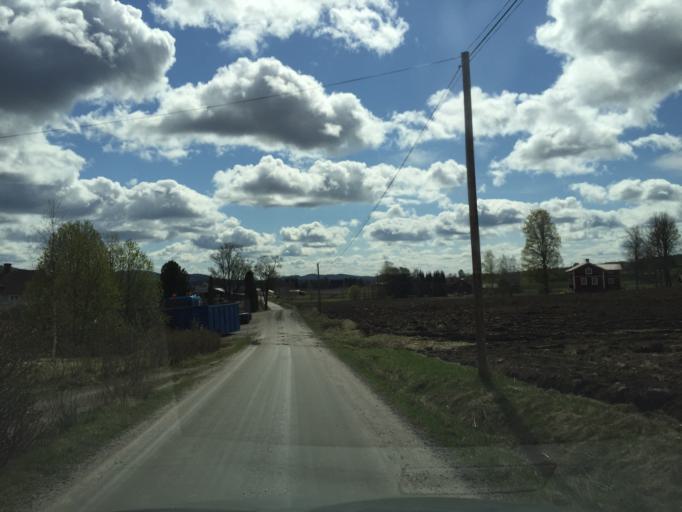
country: SE
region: Gaevleborg
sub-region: Bollnas Kommun
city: Arbra
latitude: 61.5182
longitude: 16.3501
